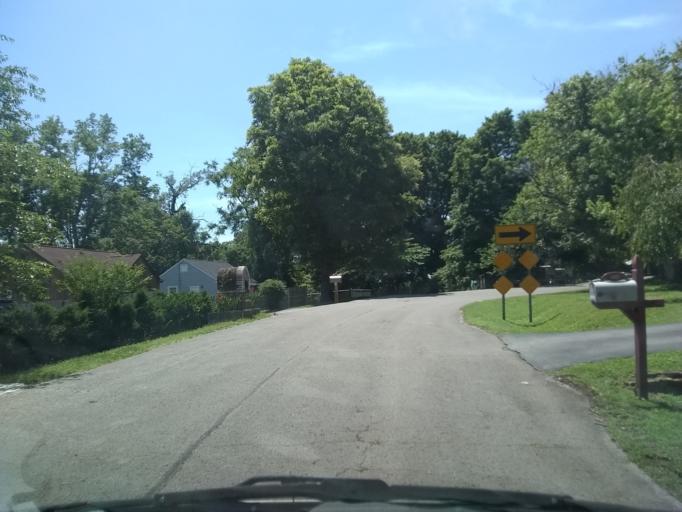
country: US
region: Tennessee
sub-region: Davidson County
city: Oak Hill
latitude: 36.1263
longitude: -86.7034
